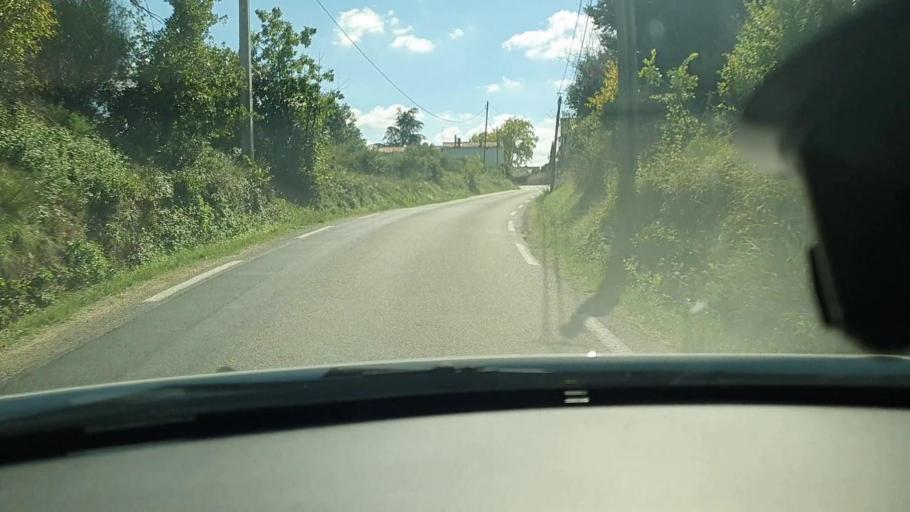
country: FR
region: Languedoc-Roussillon
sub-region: Departement du Gard
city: Goudargues
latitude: 44.1647
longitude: 4.4850
